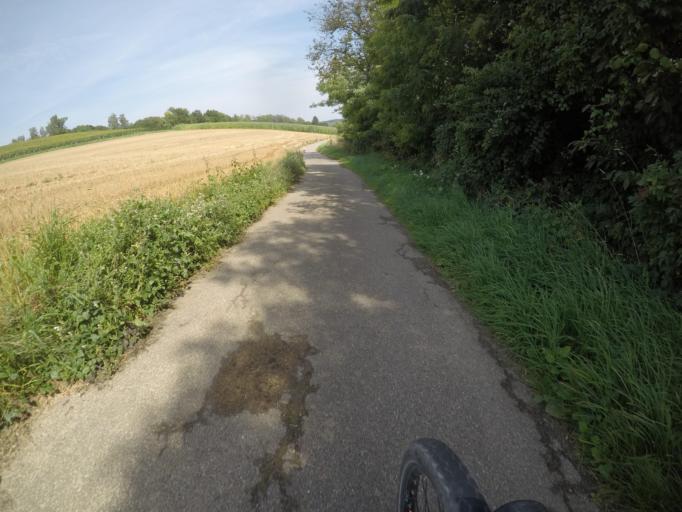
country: DE
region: Baden-Wuerttemberg
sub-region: Karlsruhe Region
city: Gondelsheim
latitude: 49.0949
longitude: 8.6346
